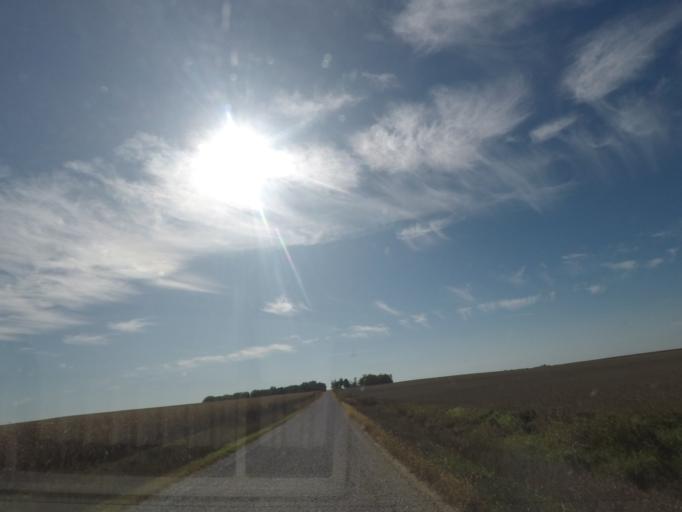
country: US
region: Iowa
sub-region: Story County
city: Nevada
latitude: 42.0554
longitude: -93.3290
